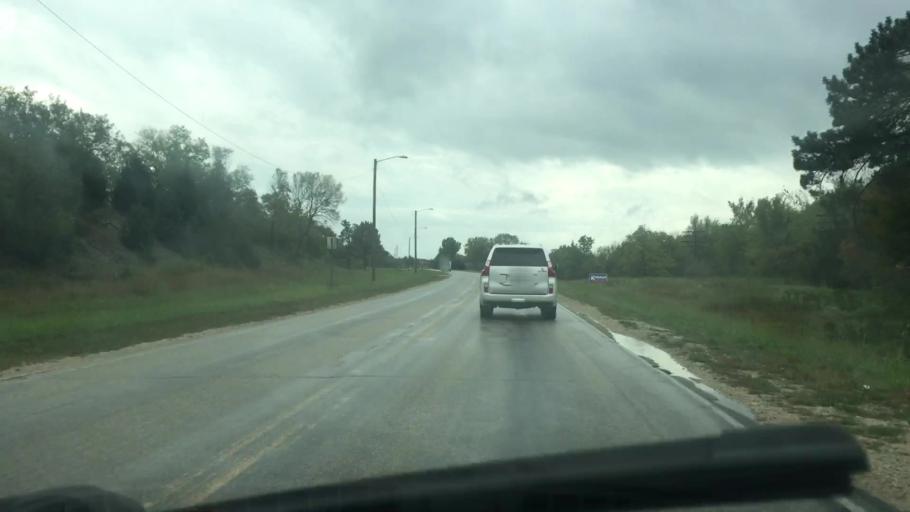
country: US
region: Kansas
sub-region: Allen County
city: Iola
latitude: 37.9071
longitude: -95.4098
